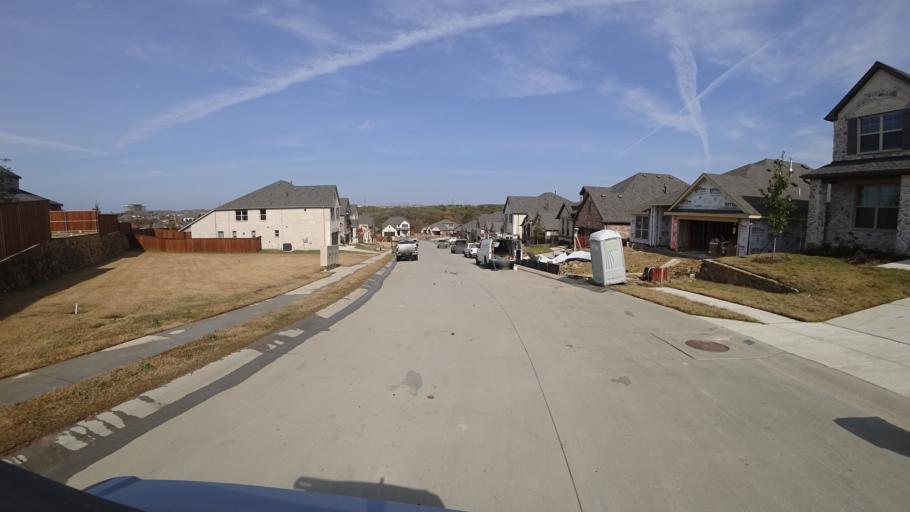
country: US
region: Texas
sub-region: Denton County
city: The Colony
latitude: 33.0481
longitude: -96.8814
